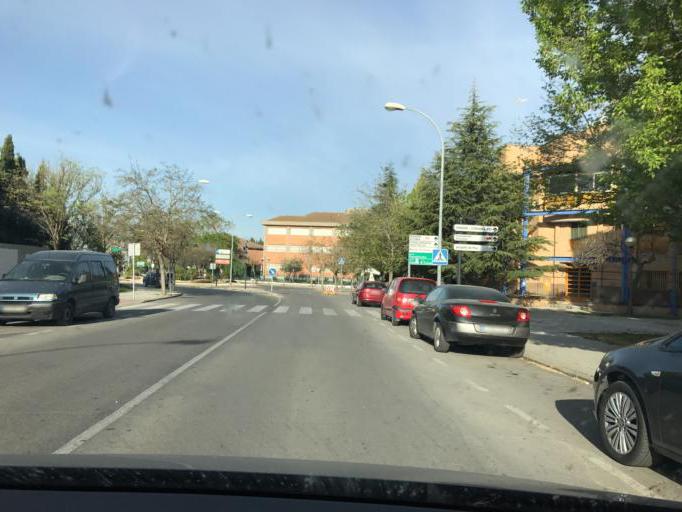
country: ES
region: Madrid
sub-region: Provincia de Madrid
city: Pinto
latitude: 40.2362
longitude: -3.6995
